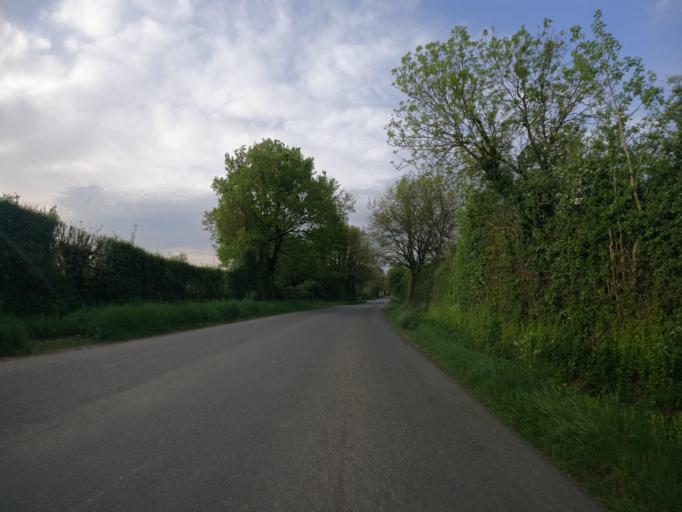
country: FR
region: Poitou-Charentes
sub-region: Departement des Deux-Sevres
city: Moncoutant
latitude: 46.7104
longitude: -0.5659
